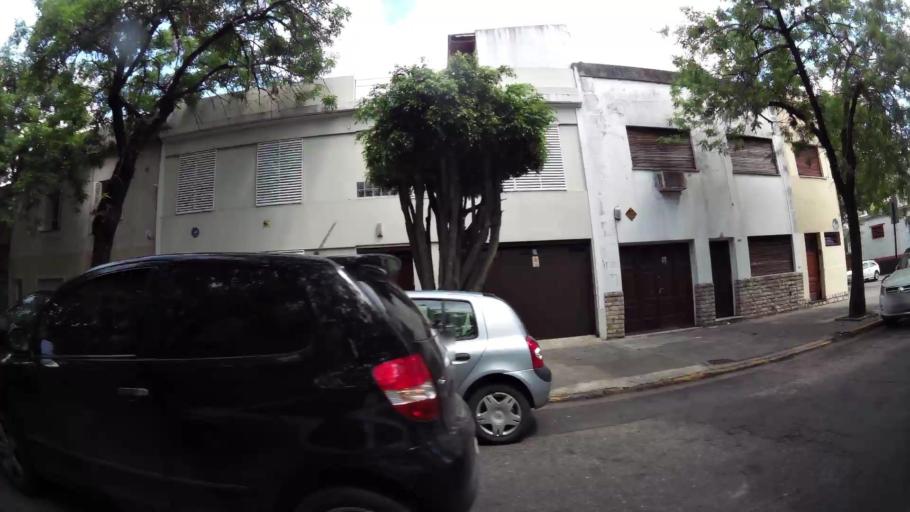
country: AR
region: Santa Fe
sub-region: Departamento de Rosario
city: Rosario
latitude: -32.9599
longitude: -60.6344
